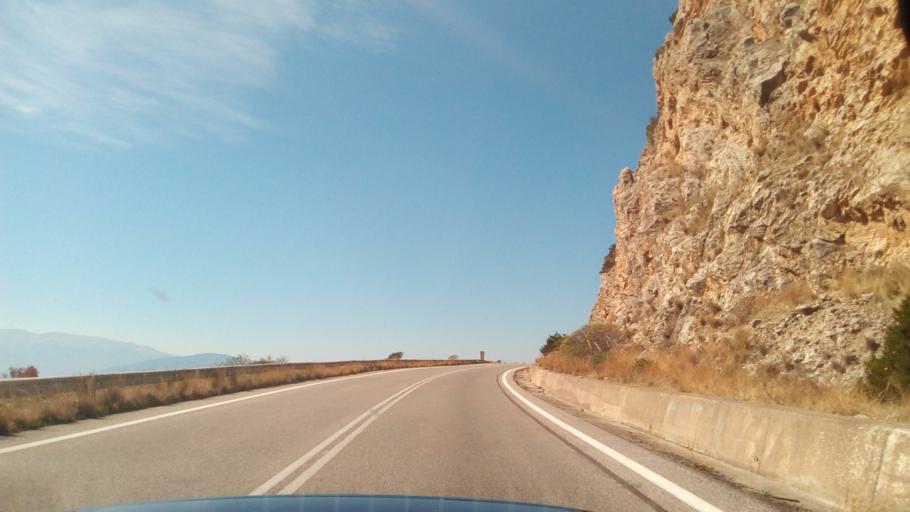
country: GR
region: West Greece
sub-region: Nomos Achaias
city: Aigio
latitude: 38.3594
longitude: 22.1346
